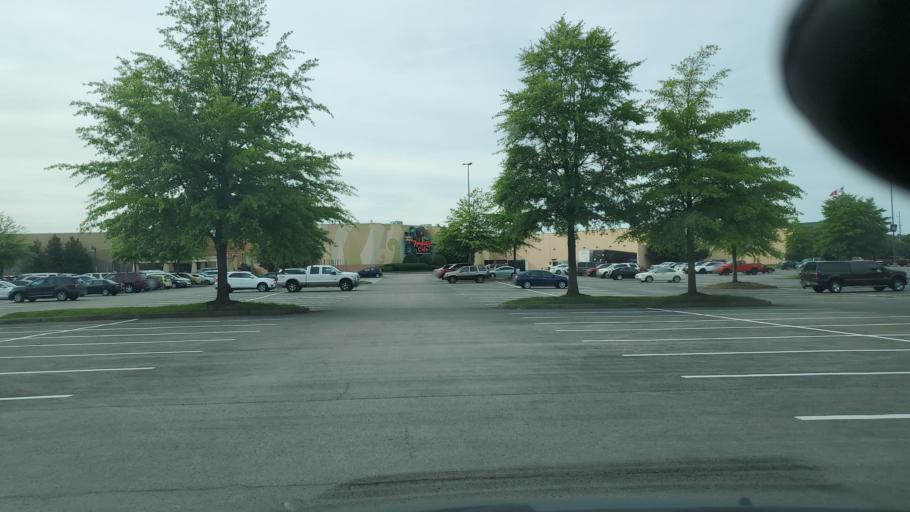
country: US
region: Tennessee
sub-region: Davidson County
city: Lakewood
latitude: 36.1989
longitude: -86.6912
